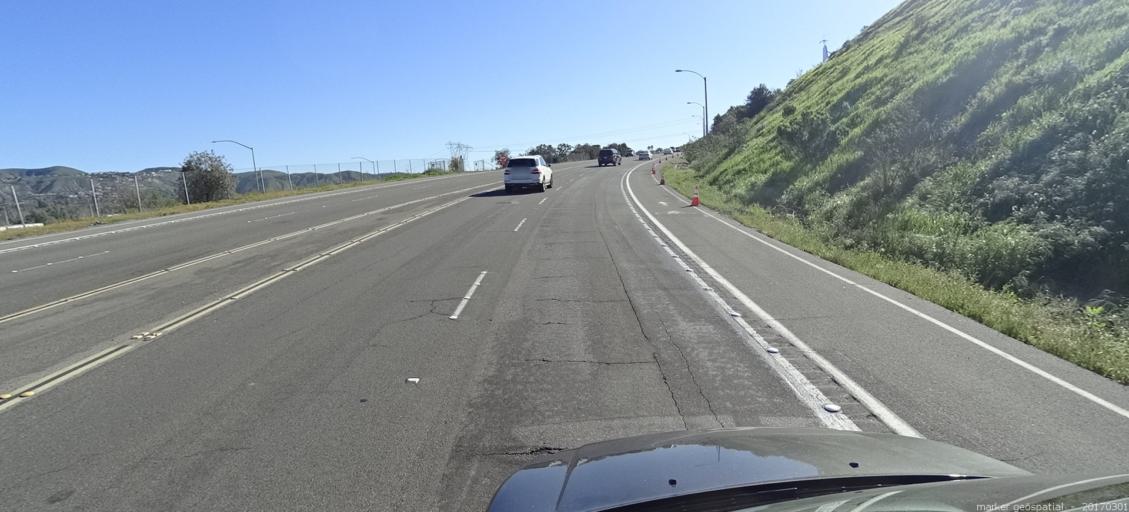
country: US
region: California
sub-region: Orange County
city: Yorba Linda
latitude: 33.8678
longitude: -117.7595
